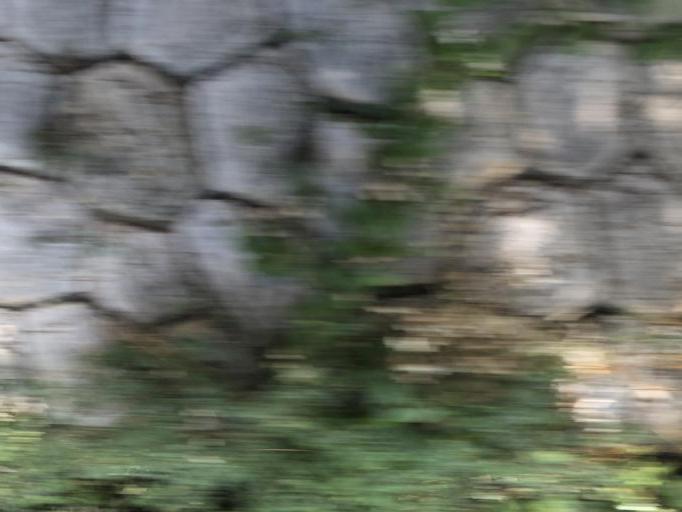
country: FR
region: Provence-Alpes-Cote d'Azur
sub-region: Departement des Alpes-Maritimes
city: Beaulieu-sur-Mer
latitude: 43.7113
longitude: 7.3217
